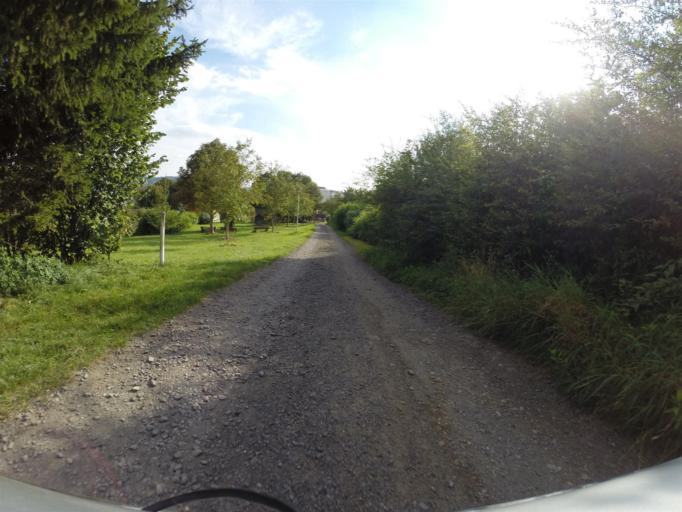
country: DE
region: Thuringia
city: Jena
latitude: 50.9549
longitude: 11.5998
